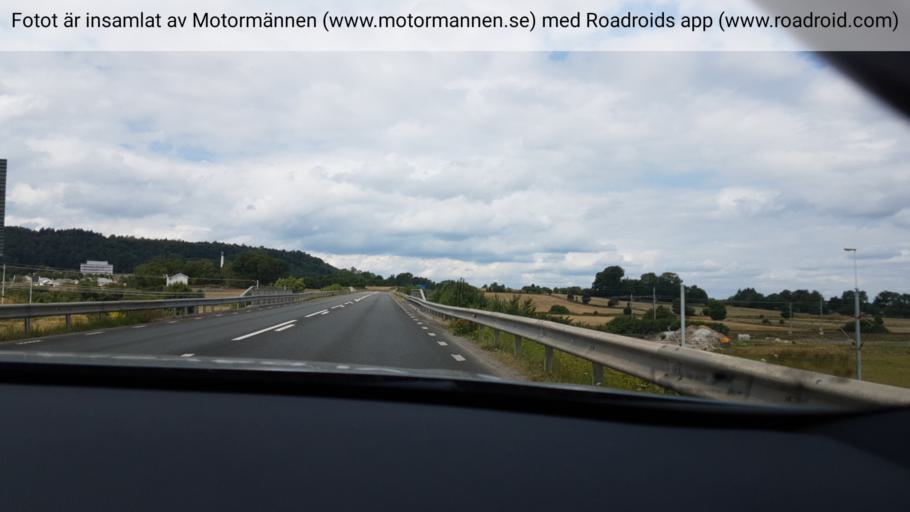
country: SE
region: Vaestra Goetaland
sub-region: Falkopings Kommun
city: Falkoeping
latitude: 58.1853
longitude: 13.5684
